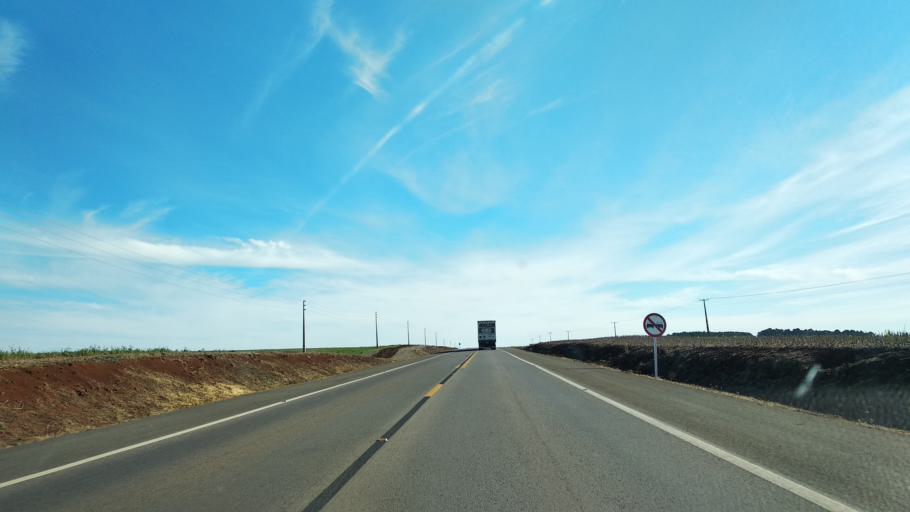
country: BR
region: Santa Catarina
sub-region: Campos Novos
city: Campos Novos
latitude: -27.4879
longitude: -51.3229
